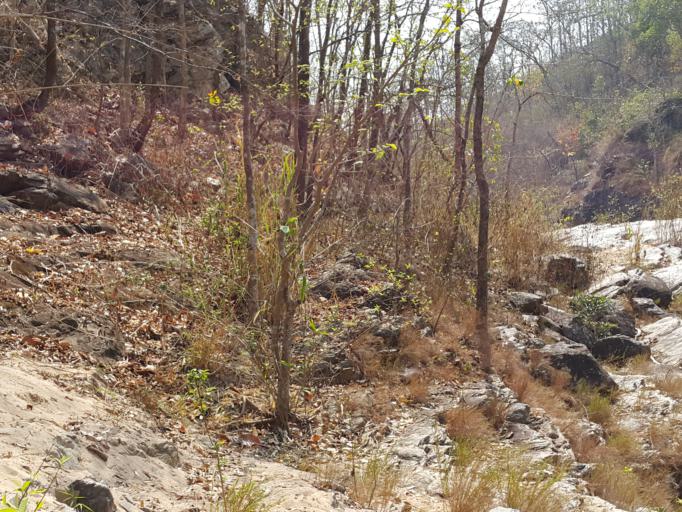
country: TH
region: Chiang Mai
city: Hang Dong
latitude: 18.7237
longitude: 98.8195
